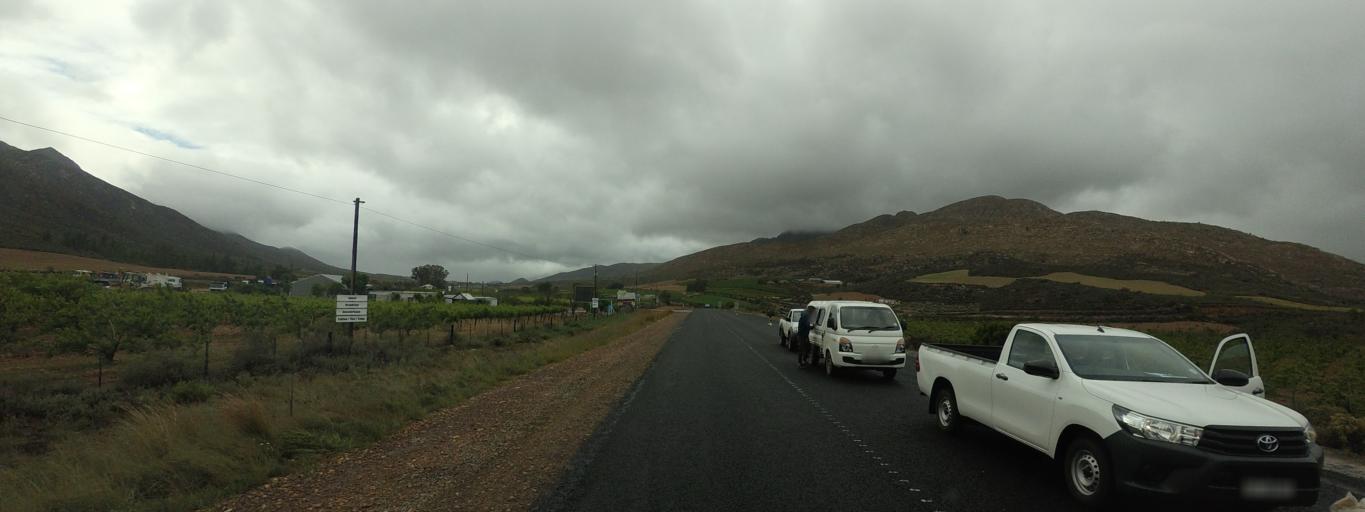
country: ZA
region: Western Cape
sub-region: Eden District Municipality
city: George
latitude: -33.8141
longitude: 22.3499
